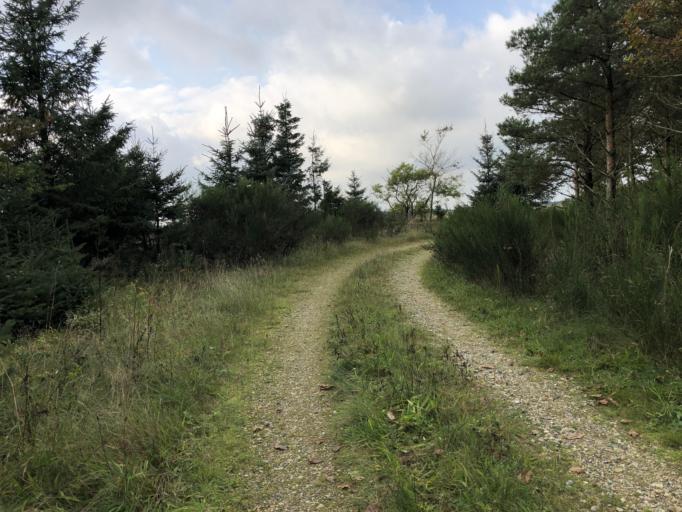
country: DK
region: Central Jutland
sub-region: Holstebro Kommune
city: Ulfborg
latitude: 56.2177
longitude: 8.4358
